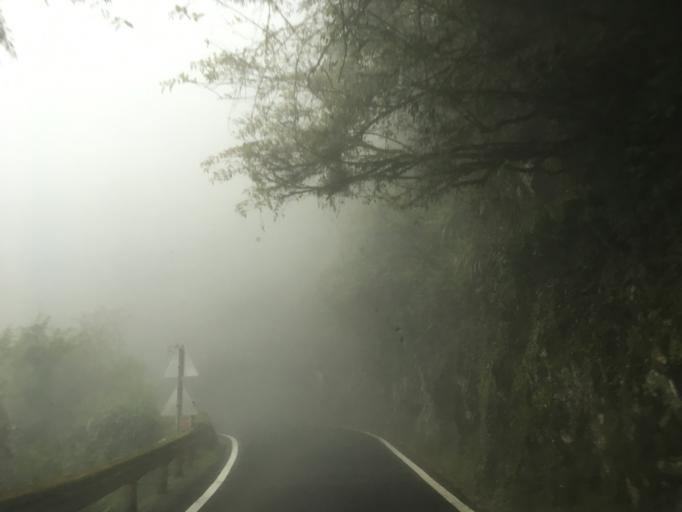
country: TW
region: Taiwan
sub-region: Hualien
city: Hualian
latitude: 24.1969
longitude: 121.4282
